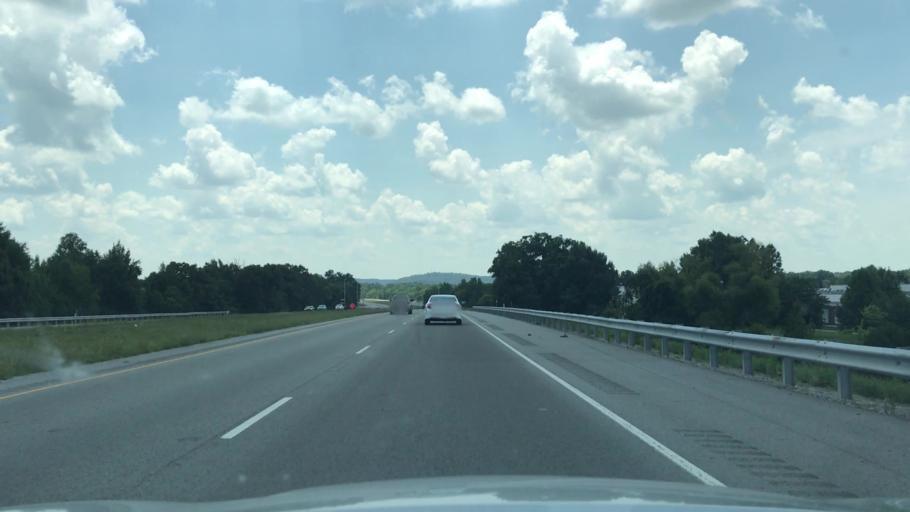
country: US
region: Tennessee
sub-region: Putnam County
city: Algood
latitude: 36.1890
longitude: -85.4621
